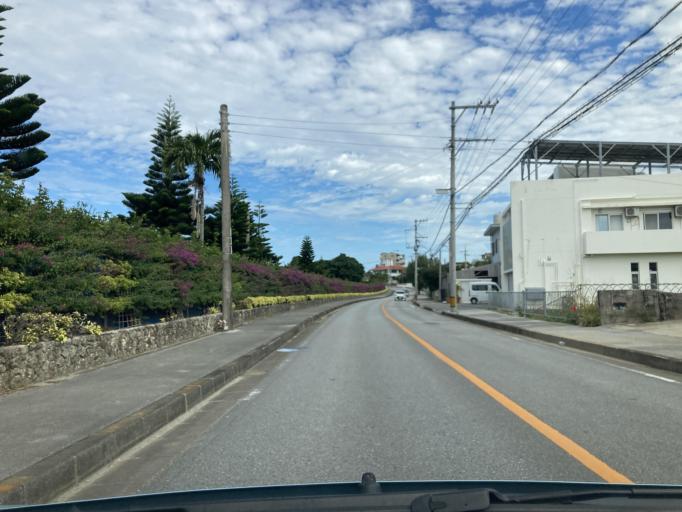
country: JP
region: Okinawa
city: Ishikawa
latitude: 26.4275
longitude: 127.7518
